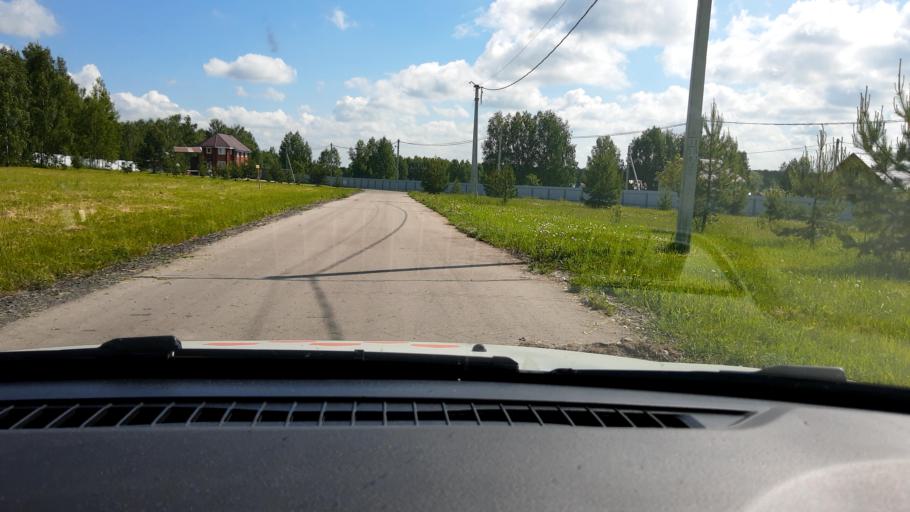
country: RU
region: Nizjnij Novgorod
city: Dal'neye Konstantinovo
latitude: 55.9316
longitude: 43.9990
